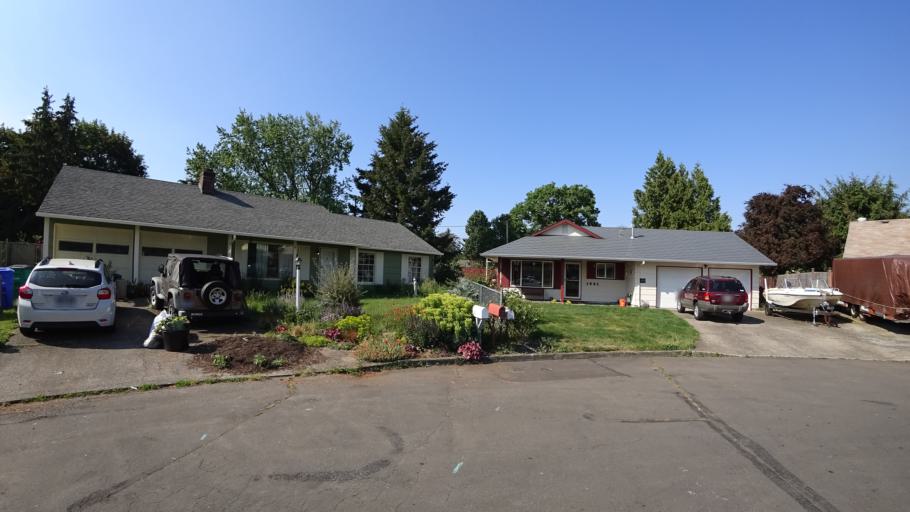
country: US
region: Oregon
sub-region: Clackamas County
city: Happy Valley
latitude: 45.5094
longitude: -122.5042
